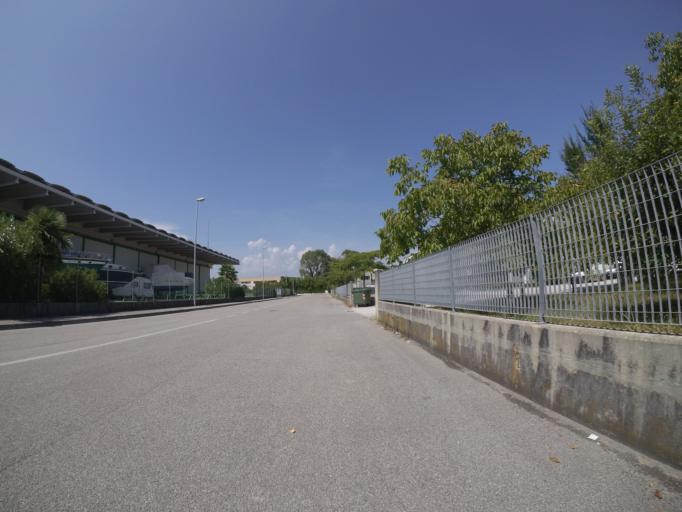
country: IT
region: Veneto
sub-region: Provincia di Venezia
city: Bibione
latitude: 45.6710
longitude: 13.0606
